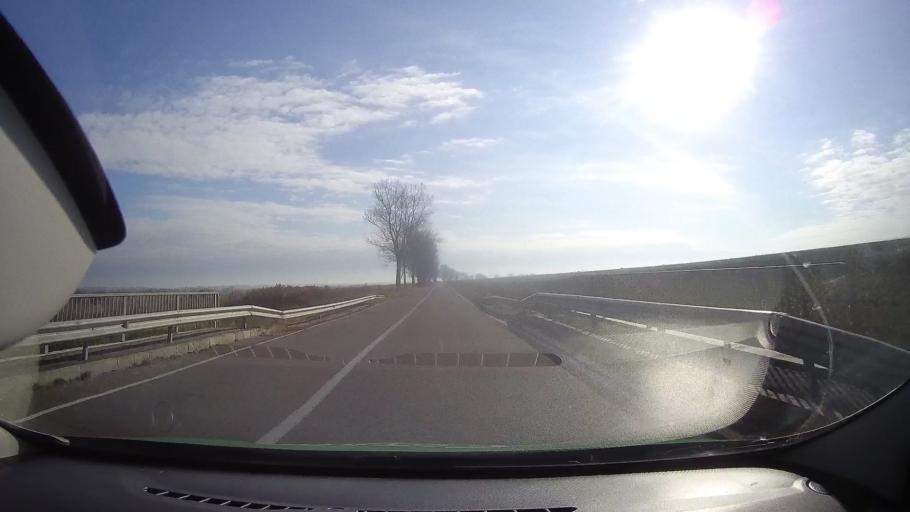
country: RO
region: Tulcea
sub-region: Comuna Mahmudia
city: Mahmudia
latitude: 45.0692
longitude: 29.1001
